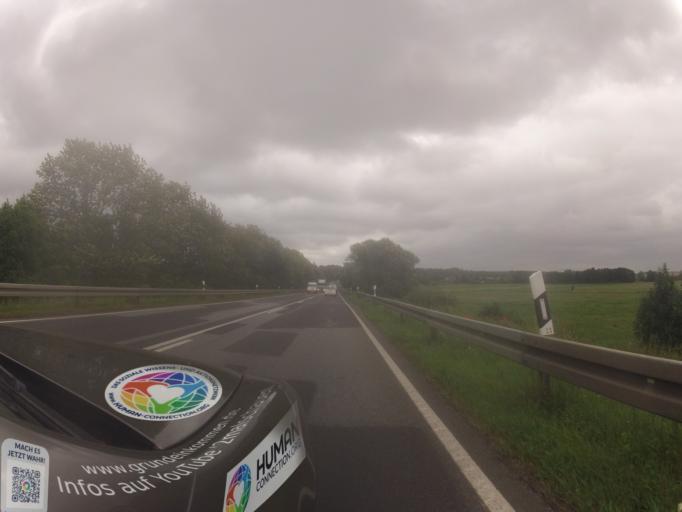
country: DE
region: Mecklenburg-Vorpommern
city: Pasewalk
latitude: 53.5044
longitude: 13.9791
